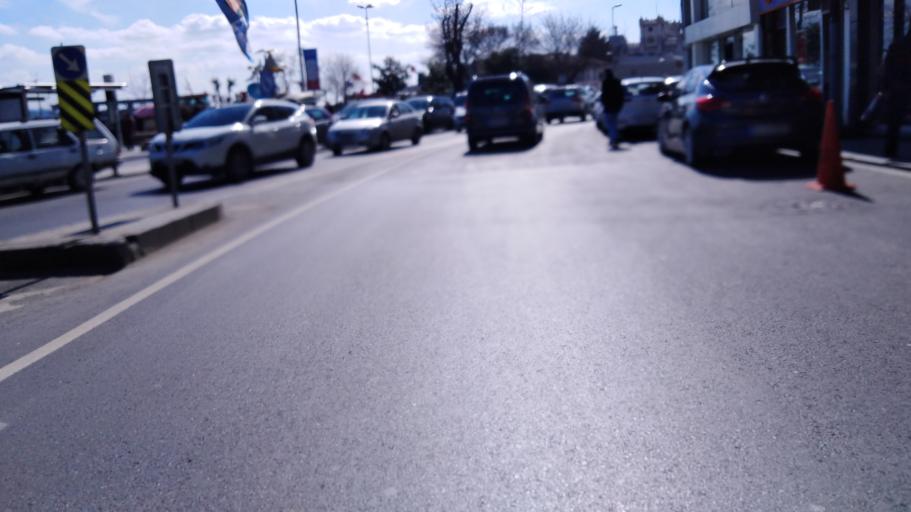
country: TR
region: Istanbul
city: Arikoey
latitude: 41.1673
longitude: 29.0572
